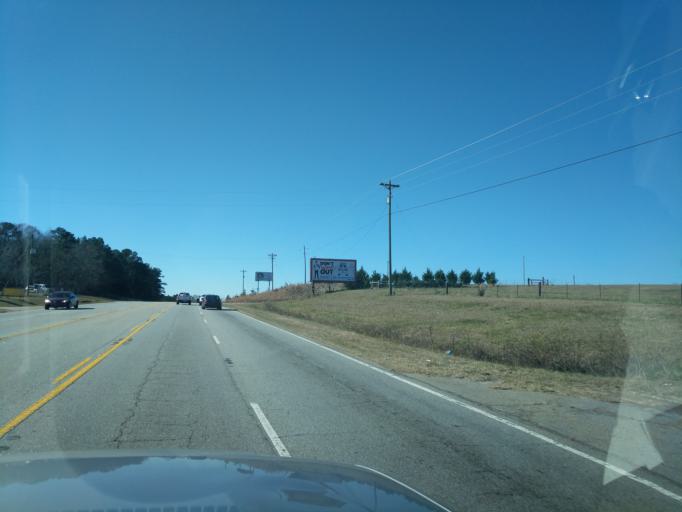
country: US
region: South Carolina
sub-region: Oconee County
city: Seneca
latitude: 34.6855
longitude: -83.0013
